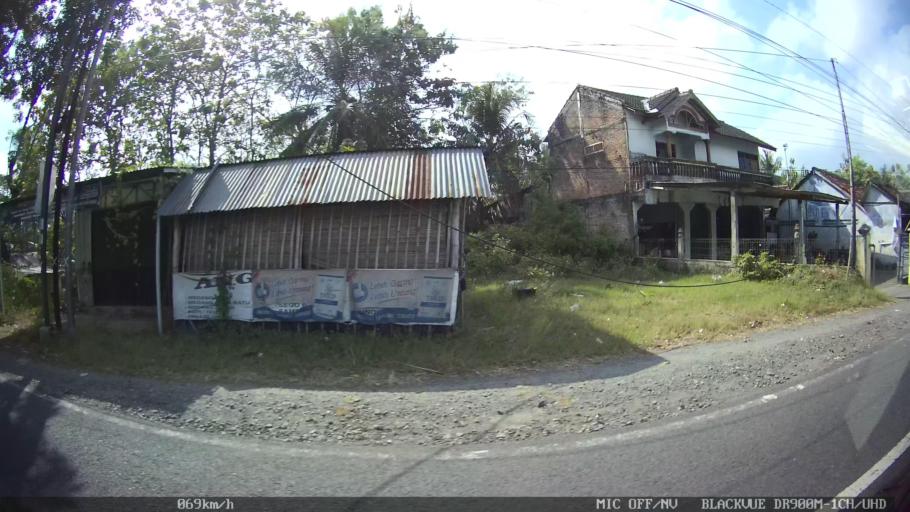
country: ID
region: Daerah Istimewa Yogyakarta
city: Srandakan
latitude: -7.8678
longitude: 110.2099
